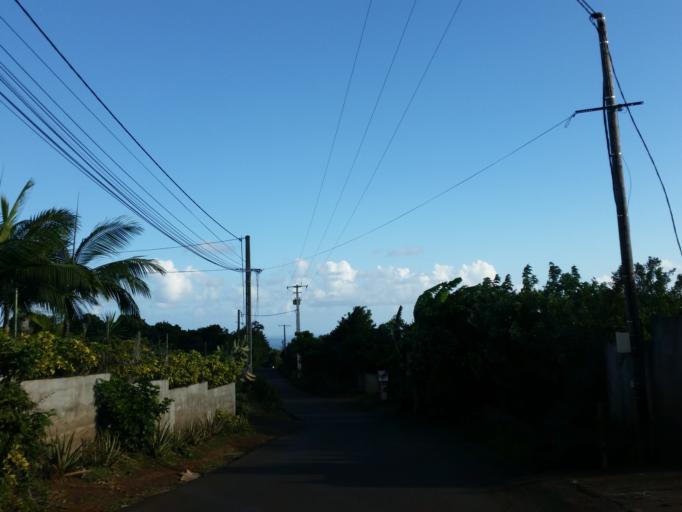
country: RE
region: Reunion
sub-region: Reunion
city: Saint-Pierre
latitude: -21.3201
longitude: 55.5024
